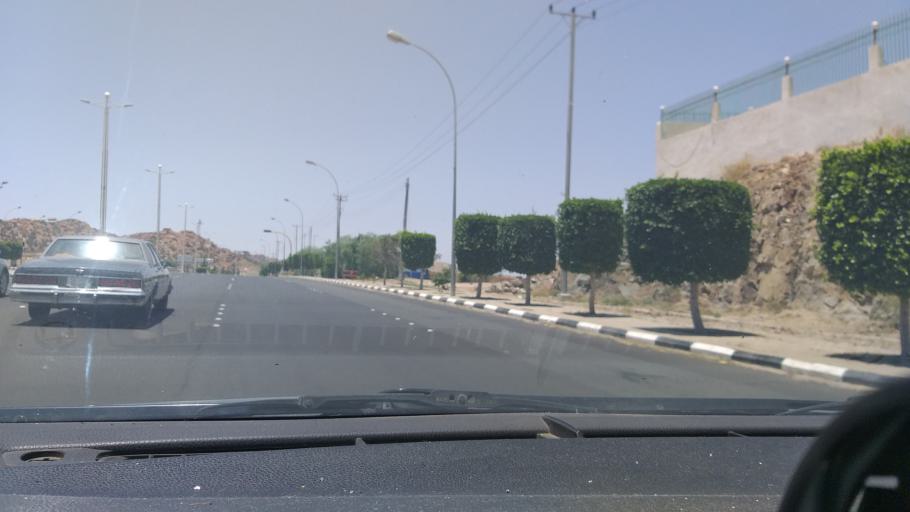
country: SA
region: Makkah
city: Al Hada
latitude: 21.3602
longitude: 40.2927
